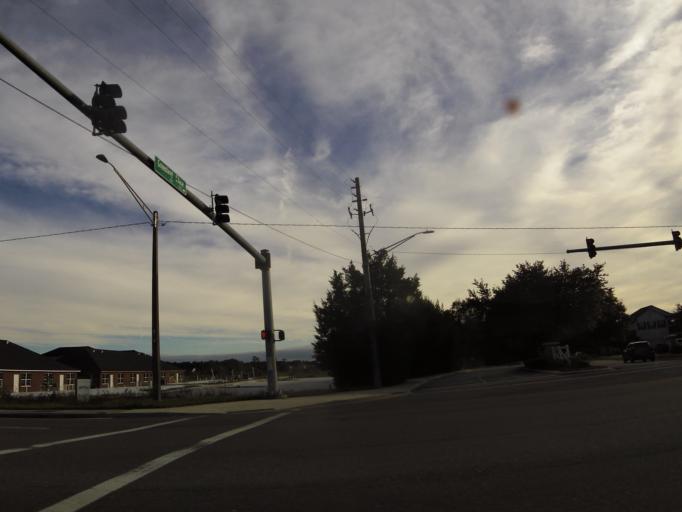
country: US
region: Florida
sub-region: Saint Johns County
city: Fruit Cove
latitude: 30.1619
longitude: -81.5479
